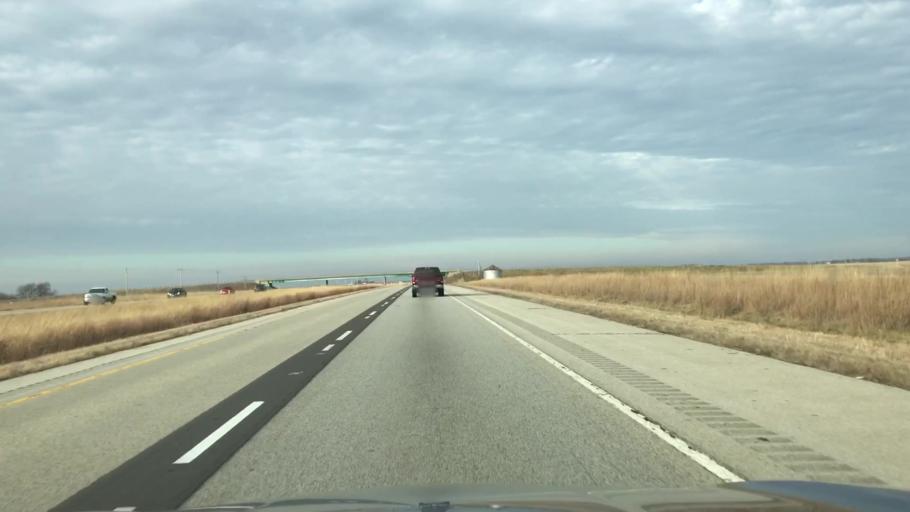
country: US
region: Illinois
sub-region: Sangamon County
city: Divernon
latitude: 39.4759
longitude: -89.6445
